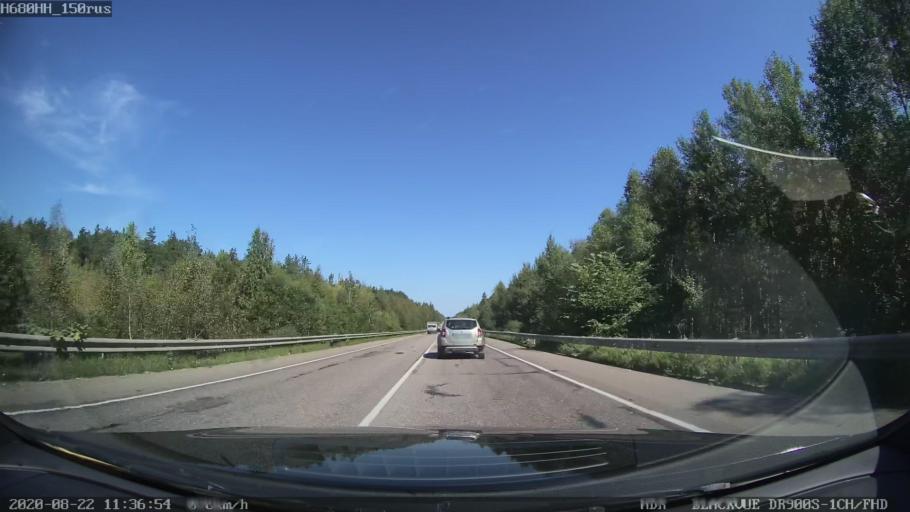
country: RU
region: Tverskaya
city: Sakharovo
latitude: 56.9396
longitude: 36.0079
